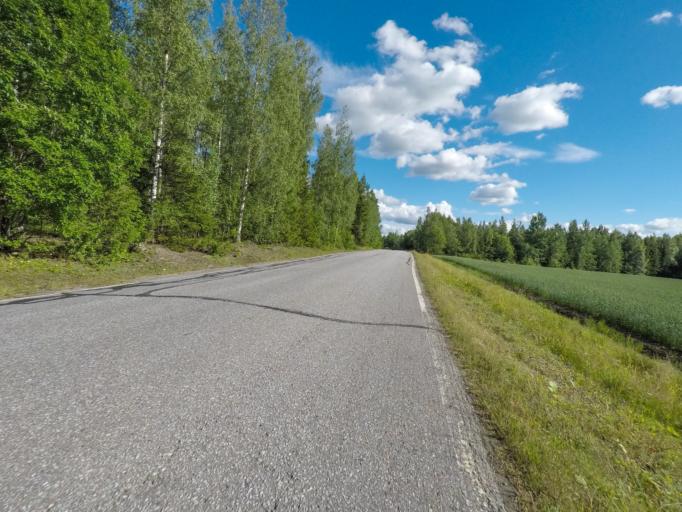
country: FI
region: South Karelia
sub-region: Imatra
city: Imatra
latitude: 61.1330
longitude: 28.6605
